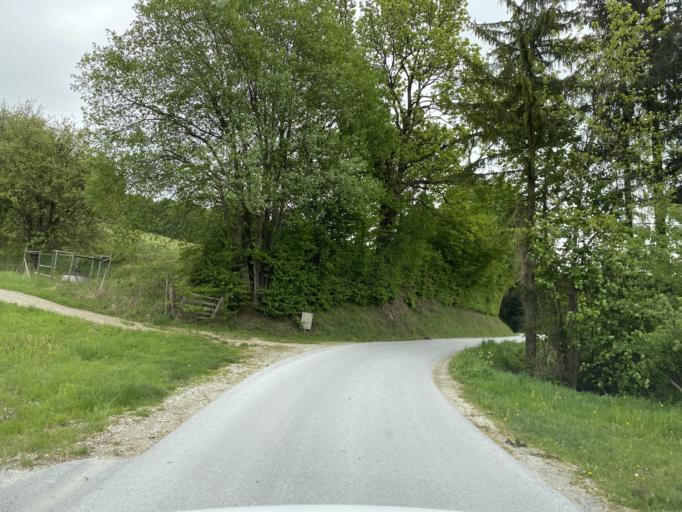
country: AT
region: Styria
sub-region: Politischer Bezirk Weiz
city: Baierdorf-Umgebung
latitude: 47.3037
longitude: 15.7011
